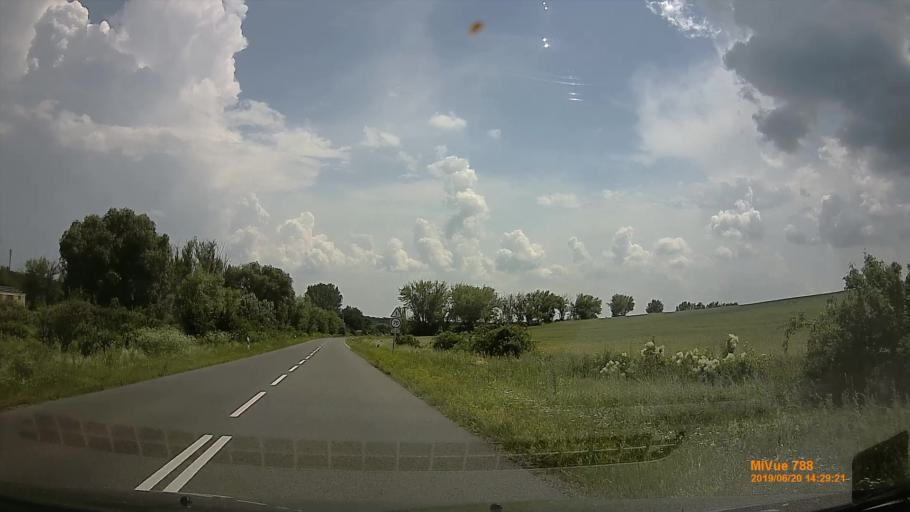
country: HU
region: Baranya
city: Hosszuheteny
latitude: 46.1606
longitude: 18.3426
